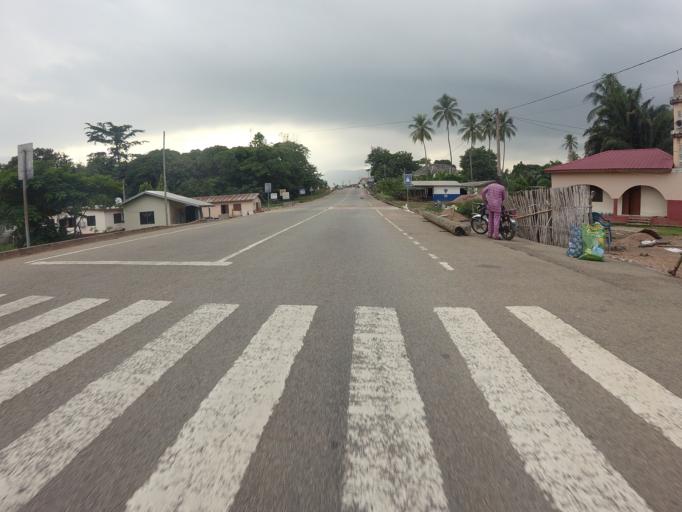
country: GH
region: Volta
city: Ho
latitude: 6.7715
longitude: 0.4803
